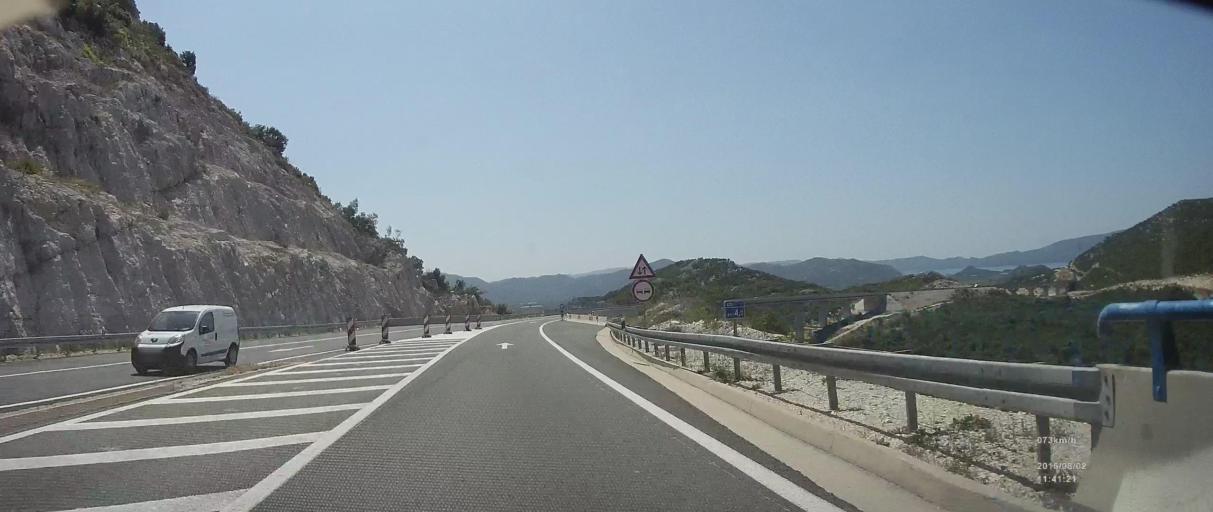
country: HR
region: Dubrovacko-Neretvanska
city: Komin
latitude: 43.0646
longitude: 17.4956
